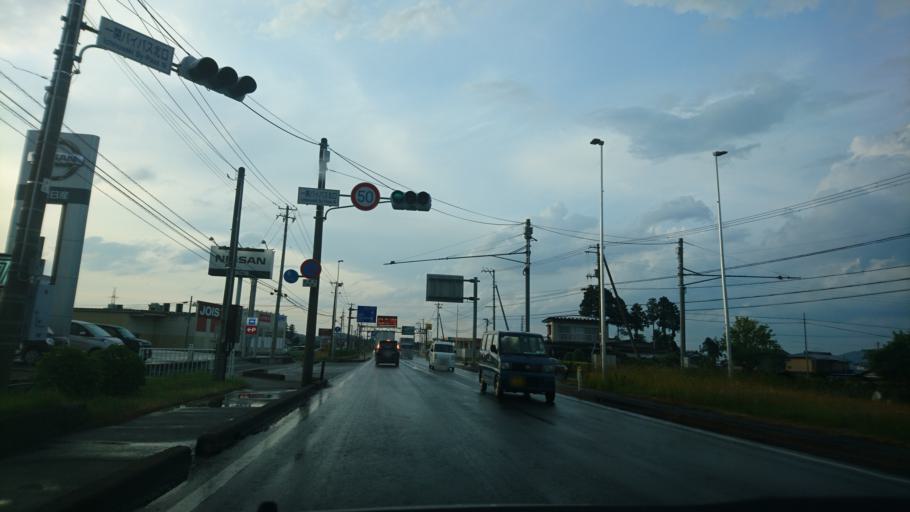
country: JP
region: Iwate
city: Ichinoseki
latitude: 38.9695
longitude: 141.1190
